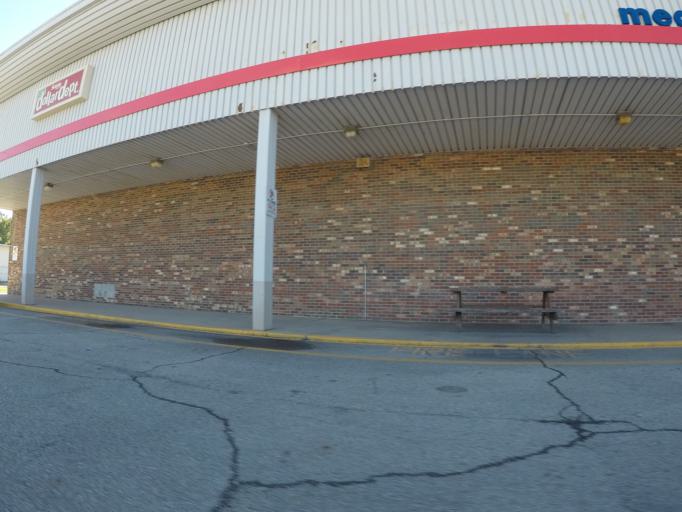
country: US
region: West Virginia
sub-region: Cabell County
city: Huntington
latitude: 38.4074
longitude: -82.4788
